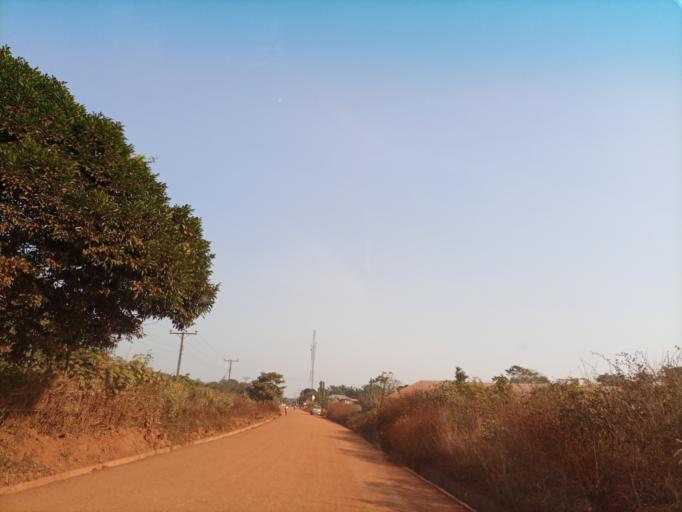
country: NG
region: Enugu
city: Opi
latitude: 6.7479
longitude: 7.4109
